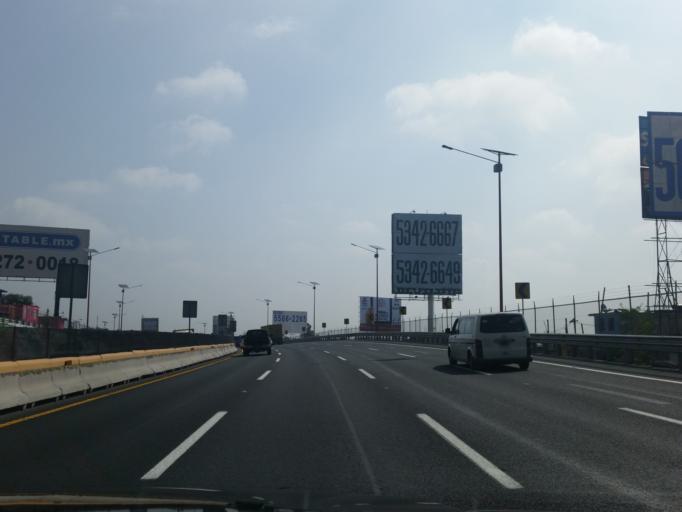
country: MX
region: Mexico
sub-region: Tlalnepantla de Baz
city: Puerto Escondido (Tepeolulco Puerto Escondido)
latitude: 19.5607
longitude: -99.0556
